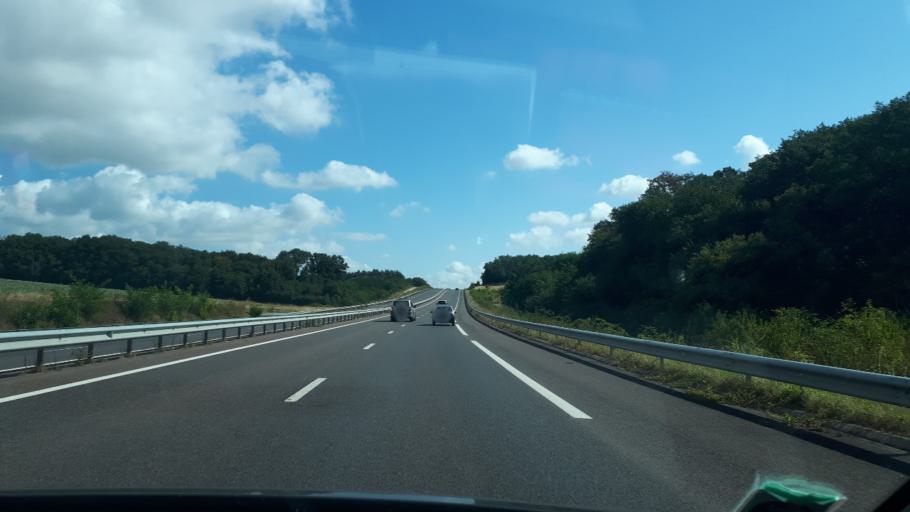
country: FR
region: Centre
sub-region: Departement du Loir-et-Cher
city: Saint-Ouen
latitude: 47.8583
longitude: 1.1118
